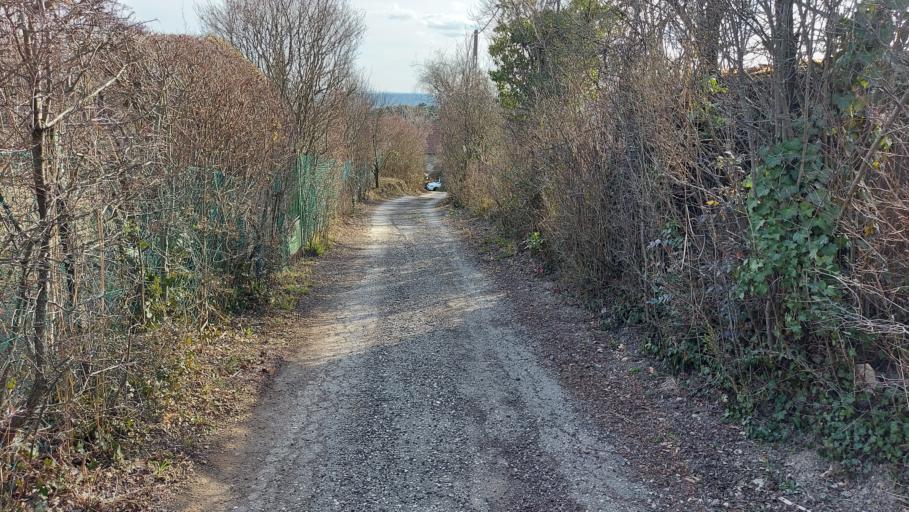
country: HU
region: Pest
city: Budaors
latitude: 47.4736
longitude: 18.9661
